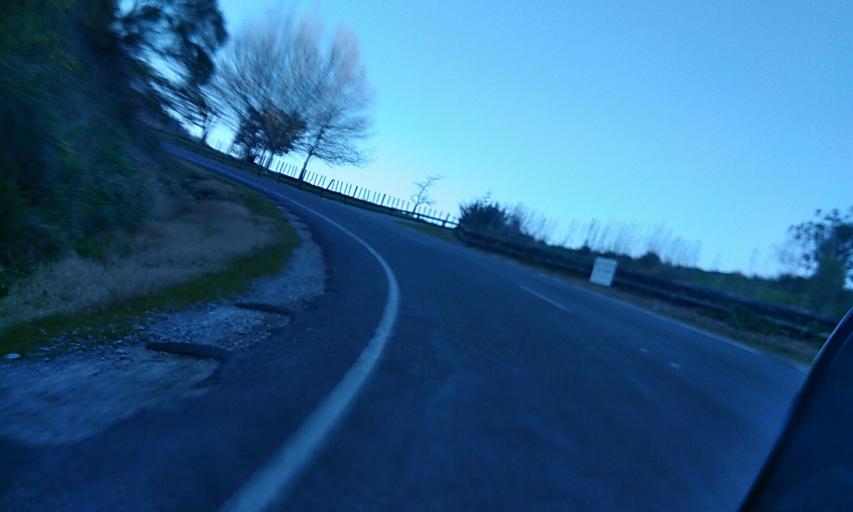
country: NZ
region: Gisborne
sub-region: Gisborne District
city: Gisborne
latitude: -38.5937
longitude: 177.9755
